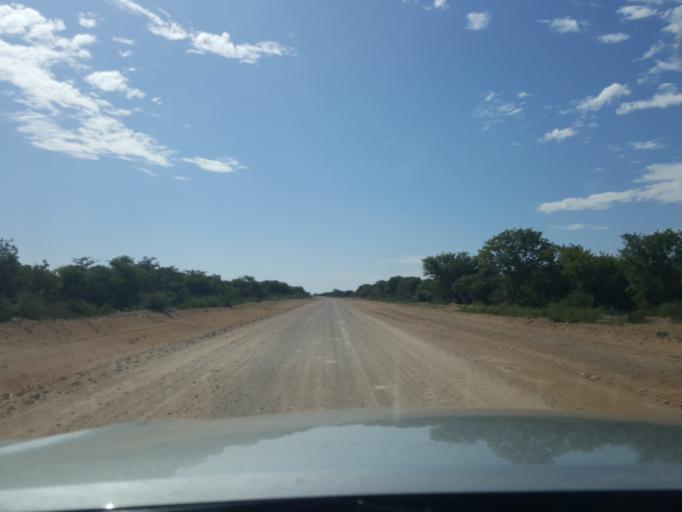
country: BW
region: Kweneng
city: Khudumelapye
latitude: -23.7905
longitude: 24.7874
